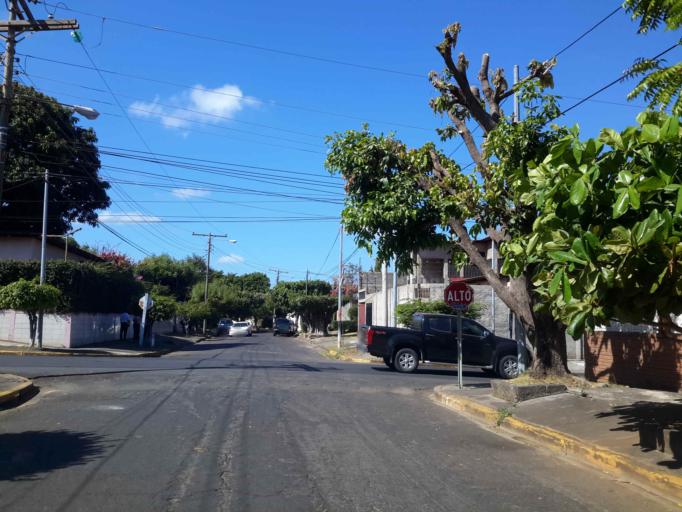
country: NI
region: Managua
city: Managua
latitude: 12.1233
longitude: -86.2697
